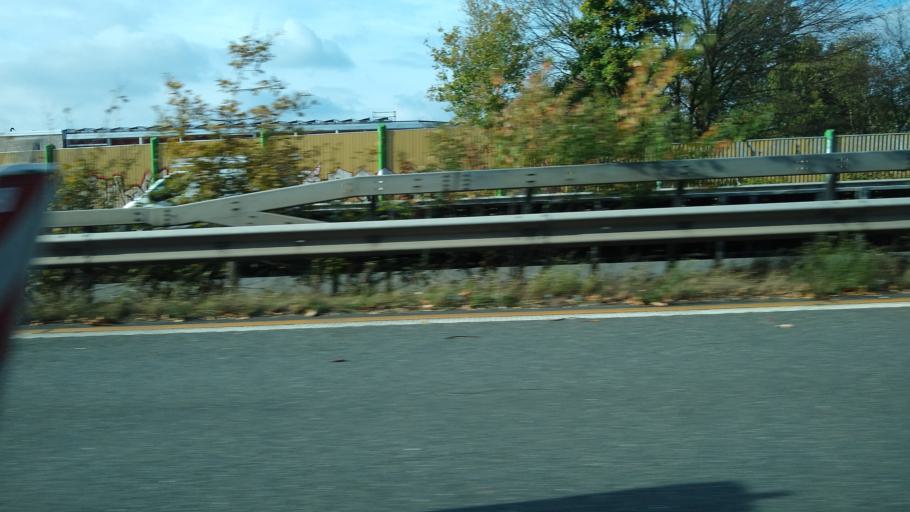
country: DE
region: Lower Saxony
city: Oldenburg
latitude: 53.1561
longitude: 8.1954
